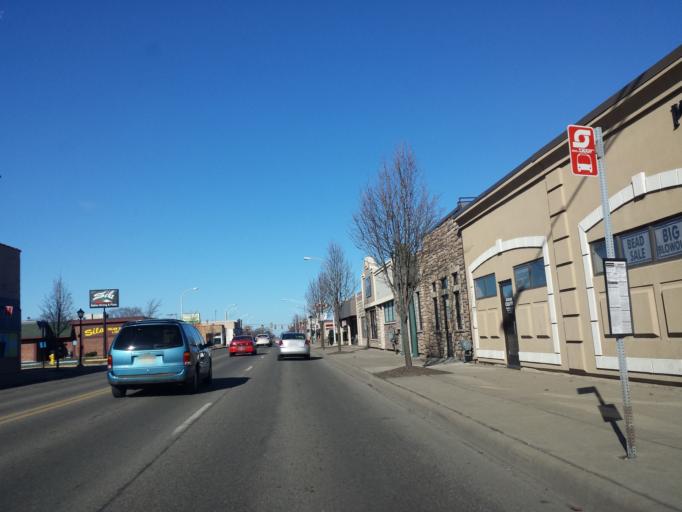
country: US
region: Michigan
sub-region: Oakland County
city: Berkley
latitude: 42.5029
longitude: -83.2002
